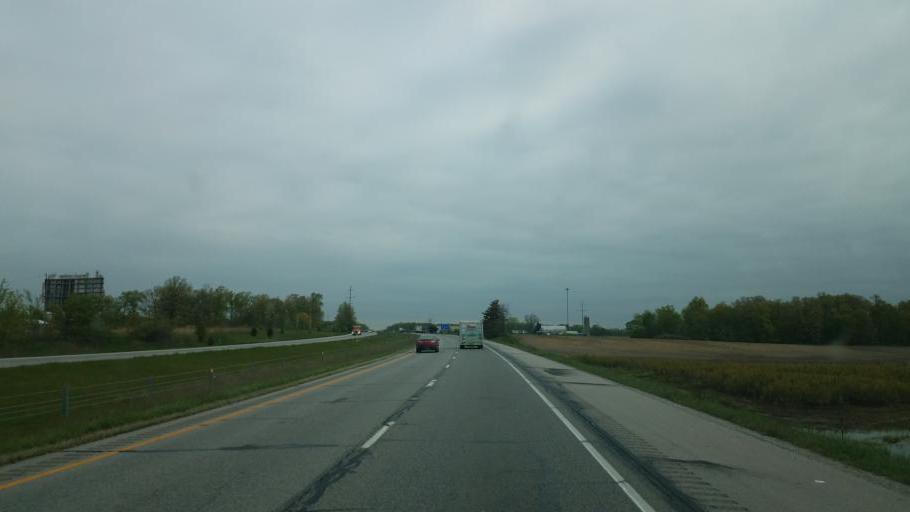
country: US
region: Indiana
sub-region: Allen County
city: Leo-Cedarville
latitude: 41.2585
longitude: -85.0870
